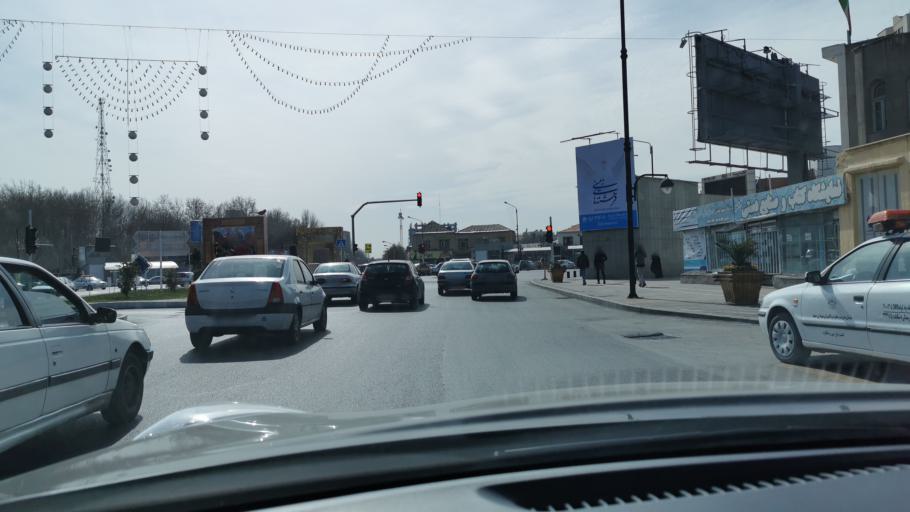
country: IR
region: Razavi Khorasan
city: Mashhad
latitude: 36.2917
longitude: 59.5853
